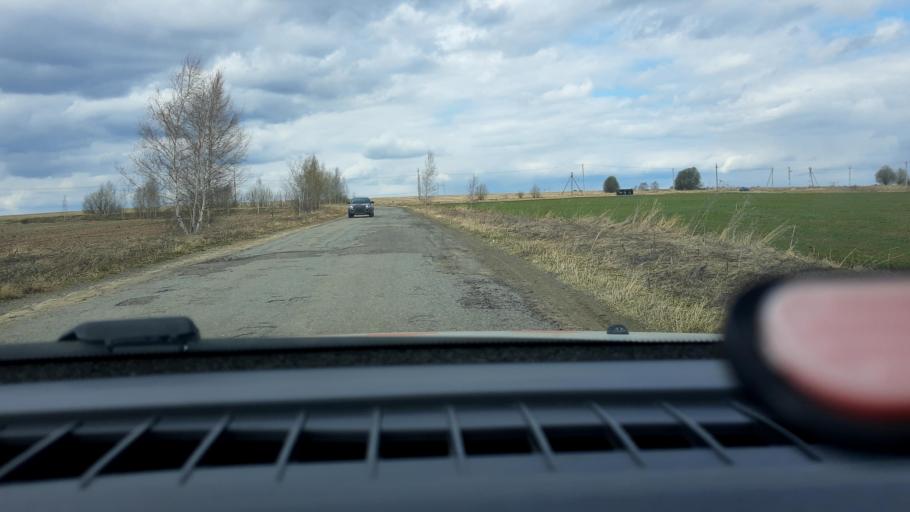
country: RU
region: Nizjnij Novgorod
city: Babino
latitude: 56.1651
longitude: 43.6871
